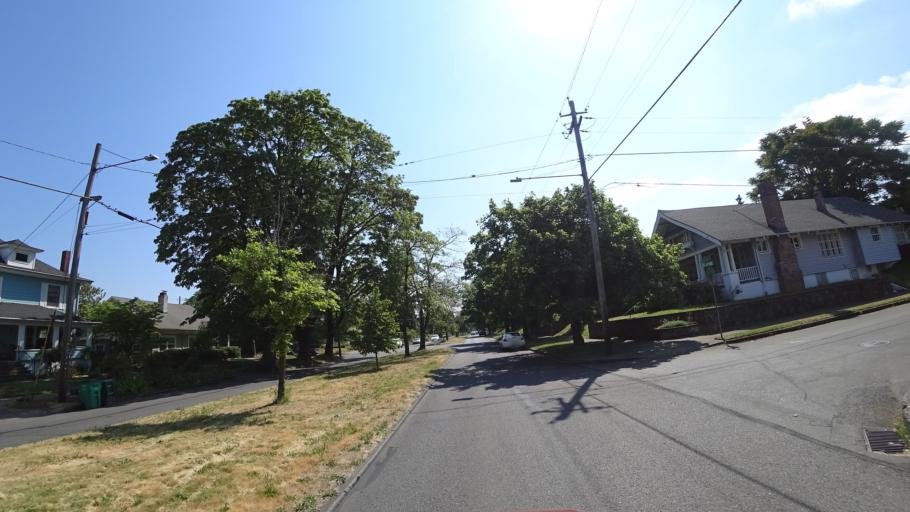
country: US
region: Oregon
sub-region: Multnomah County
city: Portland
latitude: 45.5663
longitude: -122.6581
